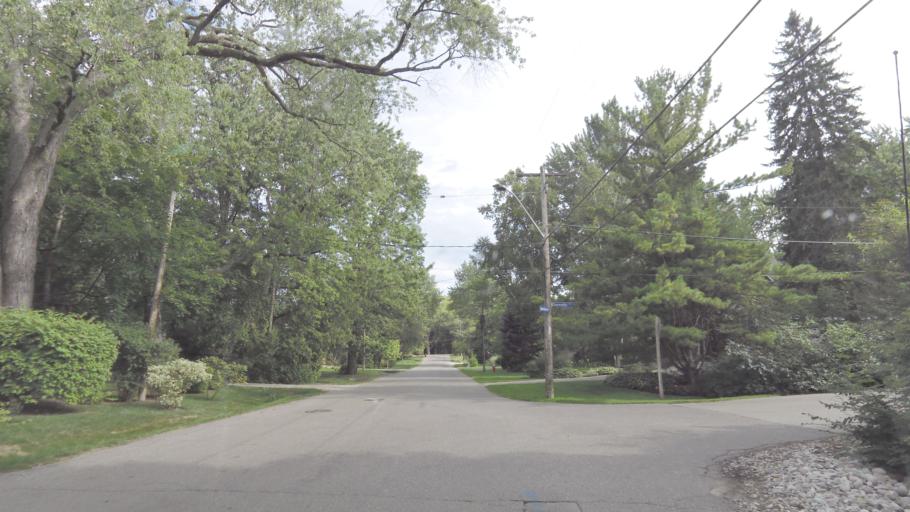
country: CA
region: Ontario
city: Mississauga
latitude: 43.5632
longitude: -79.5987
